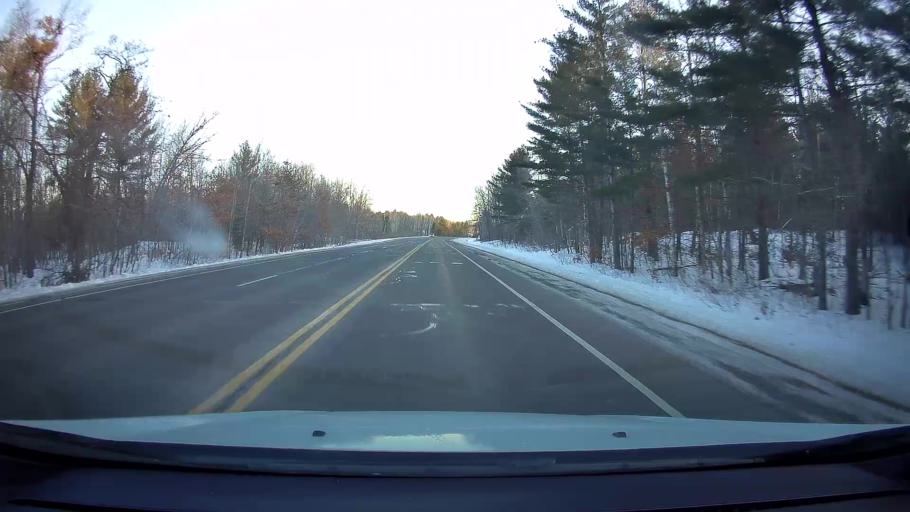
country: US
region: Wisconsin
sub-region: Barron County
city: Turtle Lake
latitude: 45.4570
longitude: -92.1017
